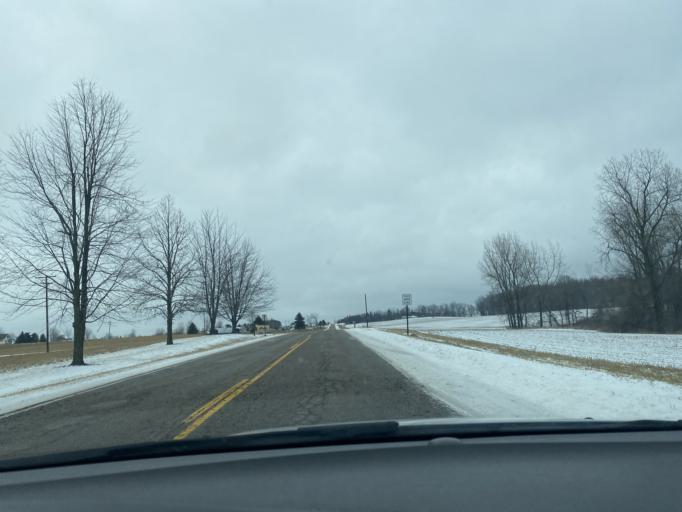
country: US
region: Michigan
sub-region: Lapeer County
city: North Branch
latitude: 43.2089
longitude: -83.1458
